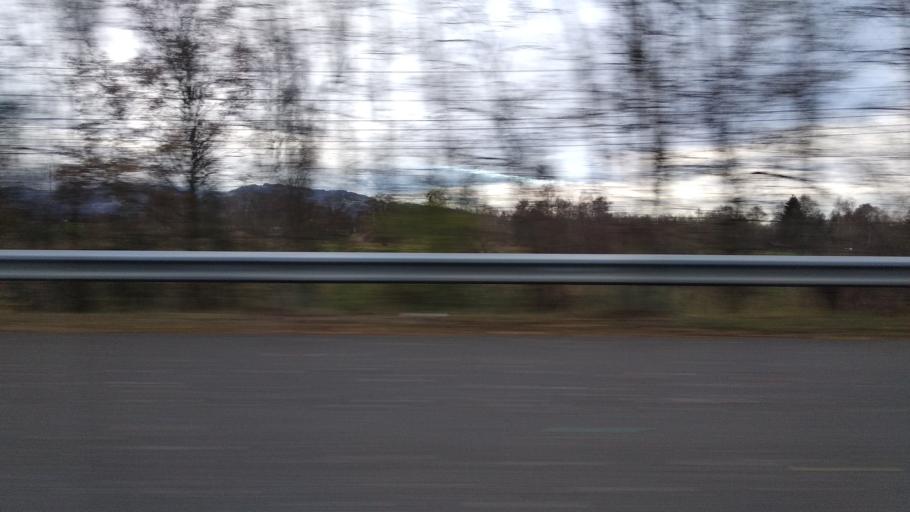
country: AT
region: Vorarlberg
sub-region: Politischer Bezirk Bregenz
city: Lauterach
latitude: 47.4552
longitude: 9.7212
